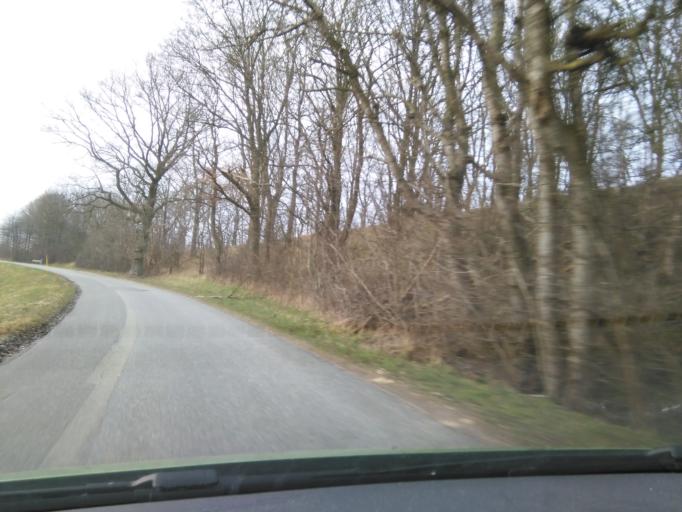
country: DK
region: Central Jutland
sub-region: Odder Kommune
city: Odder
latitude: 55.9301
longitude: 10.0941
